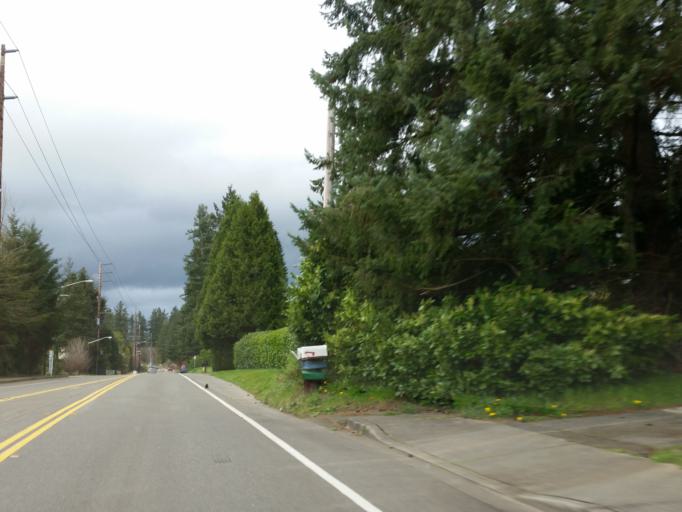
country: US
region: Washington
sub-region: King County
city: Woodinville
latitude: 47.7724
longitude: -122.1666
